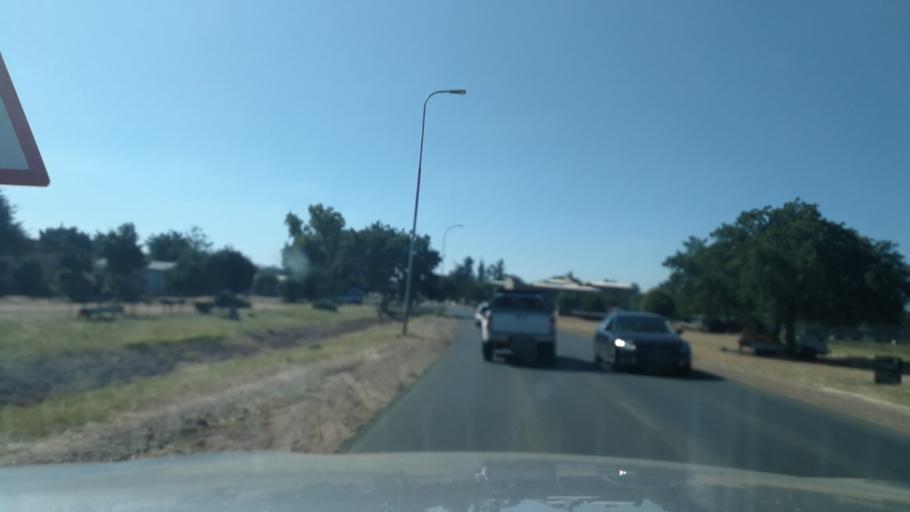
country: BW
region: South East
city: Gaborone
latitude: -24.6860
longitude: 25.9050
